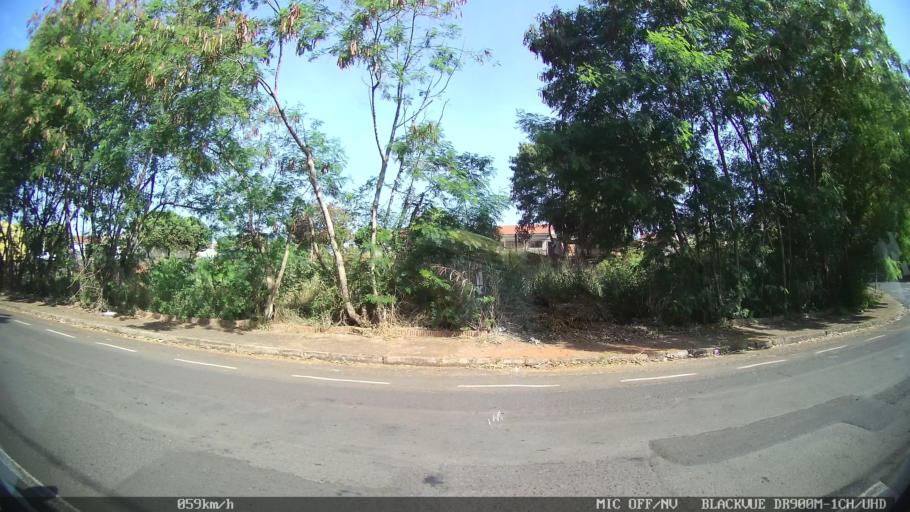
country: BR
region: Sao Paulo
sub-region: Sao Jose Do Rio Preto
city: Sao Jose do Rio Preto
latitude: -20.7918
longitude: -49.4077
